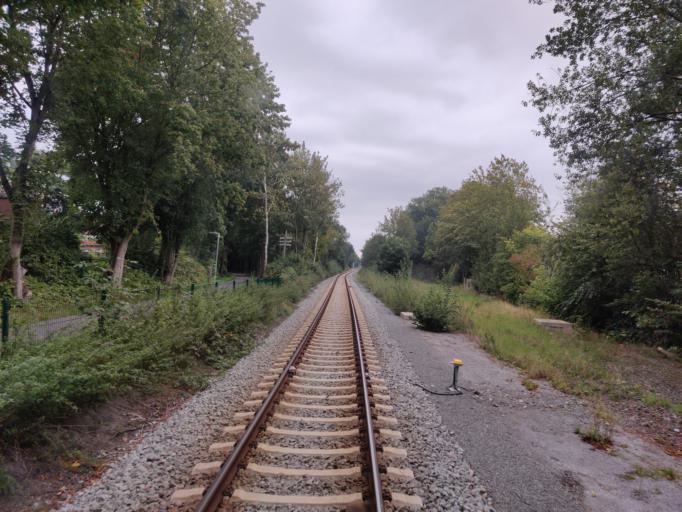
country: DE
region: Lower Saxony
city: Bremervorde
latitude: 53.4813
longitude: 9.1456
